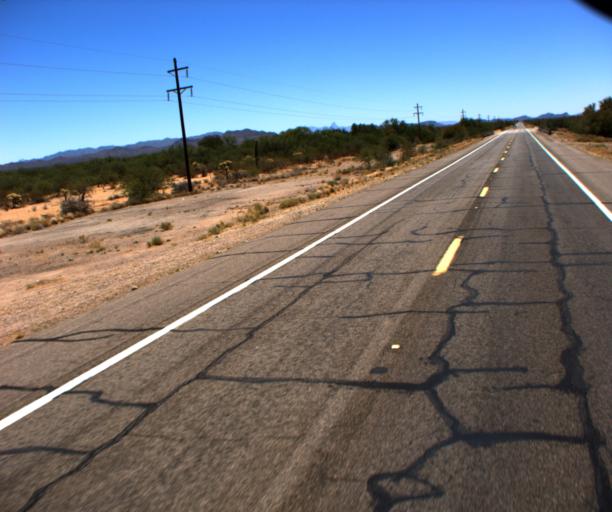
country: US
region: Arizona
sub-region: Pima County
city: Sells
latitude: 32.0919
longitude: -112.0589
